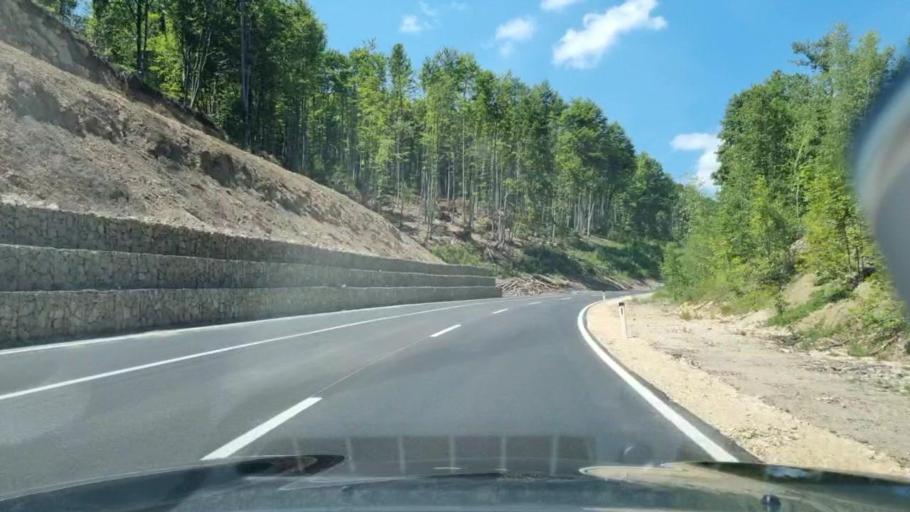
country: BA
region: Federation of Bosnia and Herzegovina
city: Velagici
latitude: 44.5453
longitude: 16.6909
